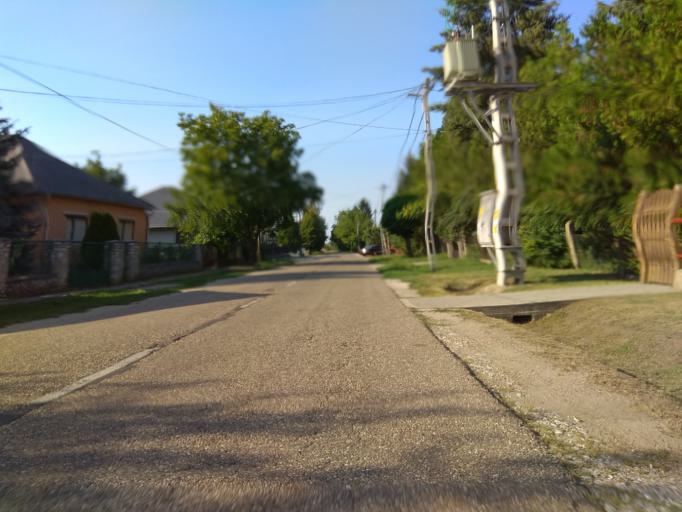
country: HU
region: Borsod-Abauj-Zemplen
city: Onod
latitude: 47.9649
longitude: 20.8836
